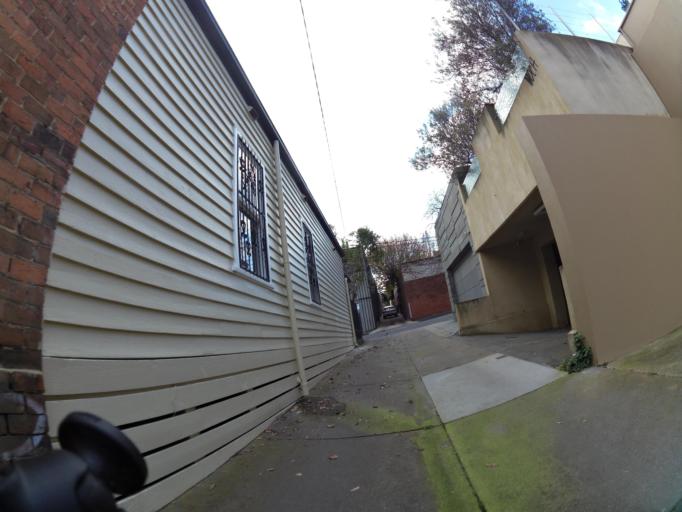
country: AU
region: Victoria
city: Albert Park
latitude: -37.8373
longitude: 144.9981
